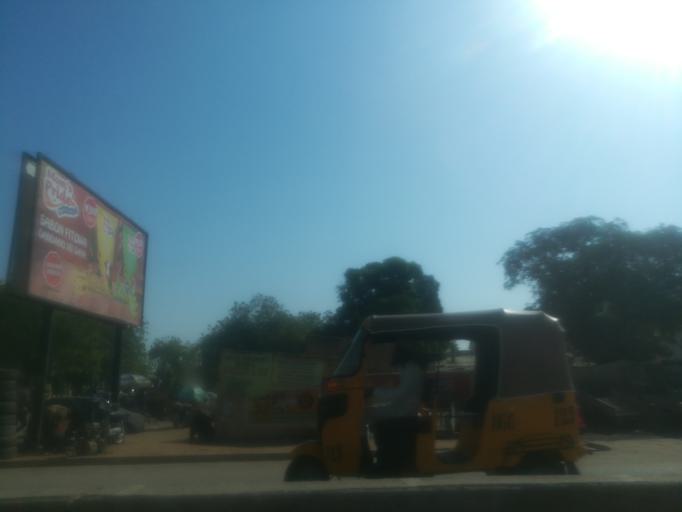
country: NG
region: Kano
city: Kano
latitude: 12.0226
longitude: 8.5346
